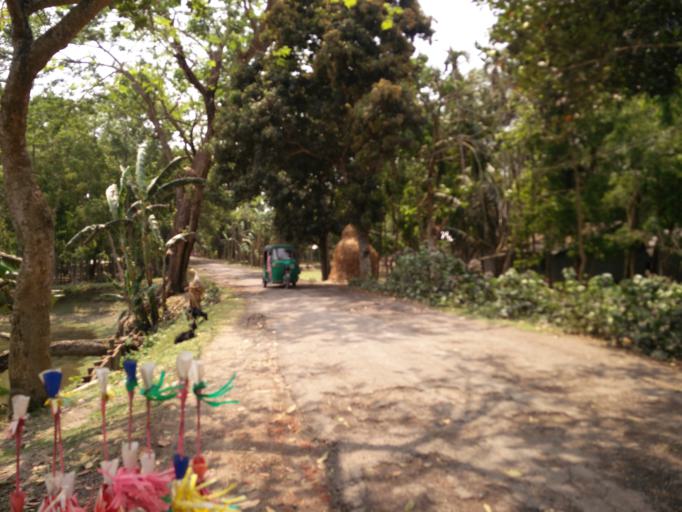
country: BD
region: Dhaka
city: Sherpur
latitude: 24.9495
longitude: 90.1618
